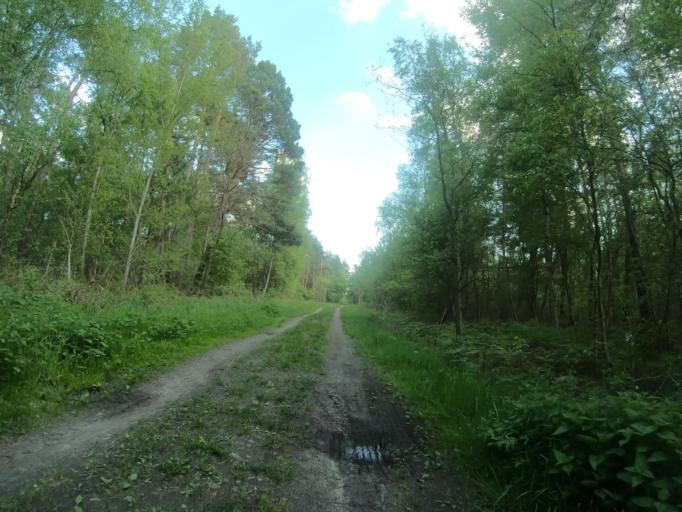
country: DE
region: Lower Saxony
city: Sassenburg
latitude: 52.5263
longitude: 10.6186
